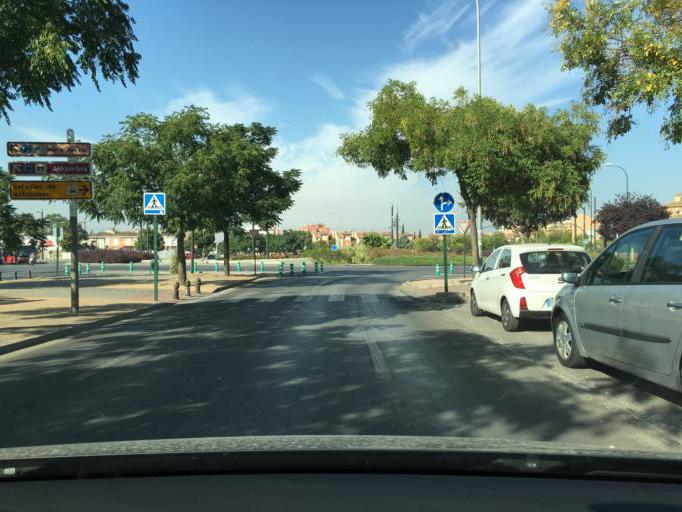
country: ES
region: Andalusia
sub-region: Provincia de Granada
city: Granada
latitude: 37.1955
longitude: -3.6143
